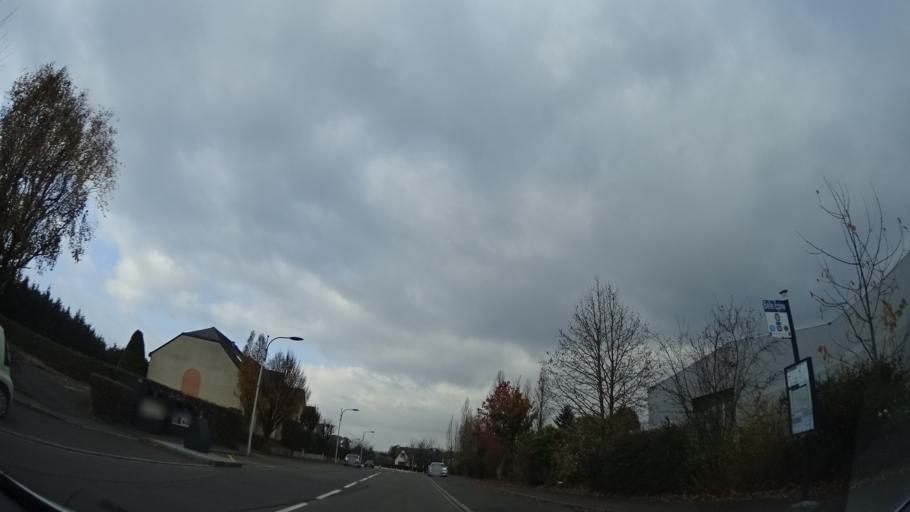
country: FR
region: Brittany
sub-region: Departement d'Ille-et-Vilaine
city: Montgermont
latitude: 48.1556
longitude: -1.7108
